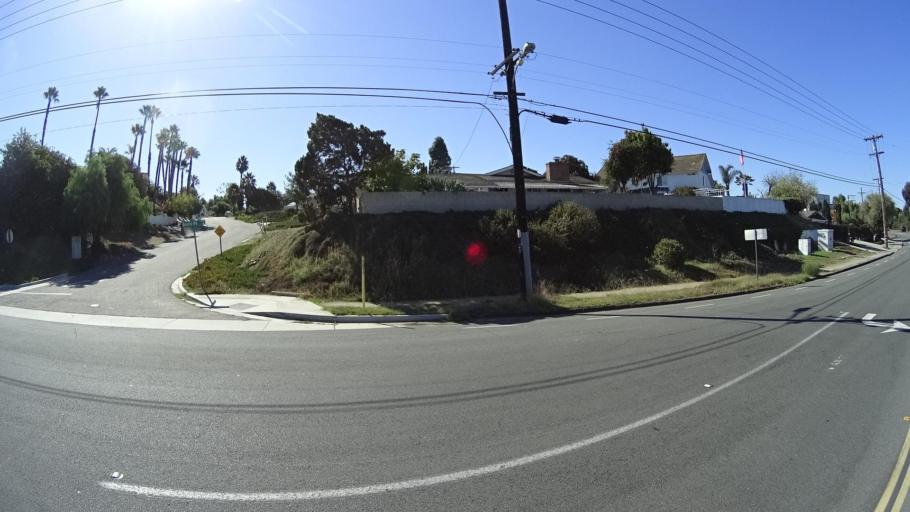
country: US
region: California
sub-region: San Diego County
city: Bonita
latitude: 32.6743
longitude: -117.0171
